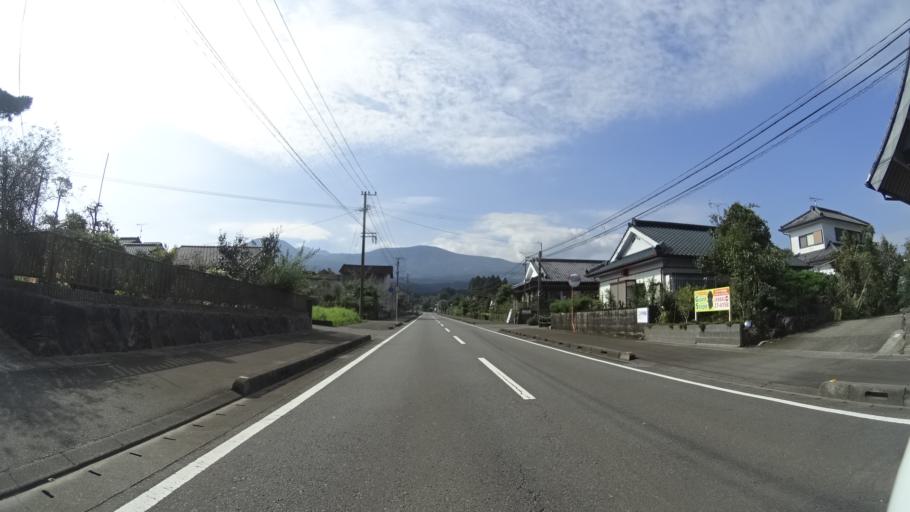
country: JP
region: Miyazaki
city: Kobayashi
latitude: 32.0160
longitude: 130.8317
